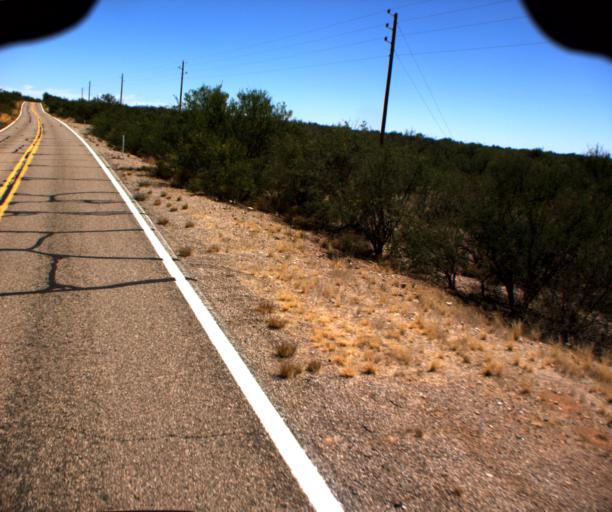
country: US
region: Arizona
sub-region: Pima County
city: Three Points
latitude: 31.8600
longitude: -111.3986
